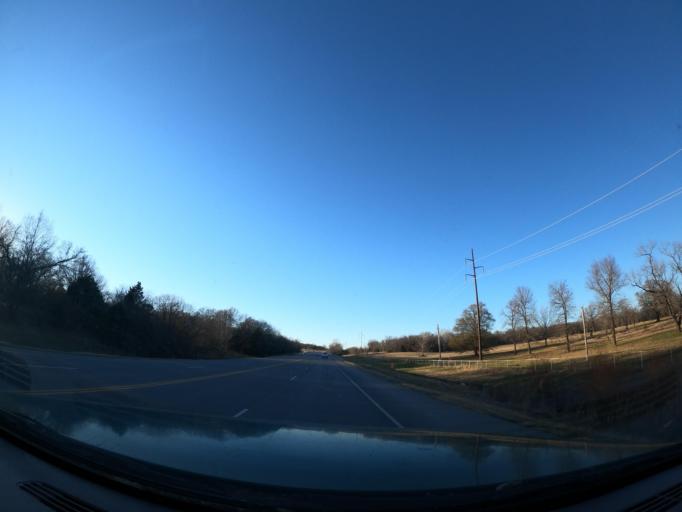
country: US
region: Oklahoma
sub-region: Pittsburg County
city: Hartshorne
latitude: 34.8909
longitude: -95.6200
